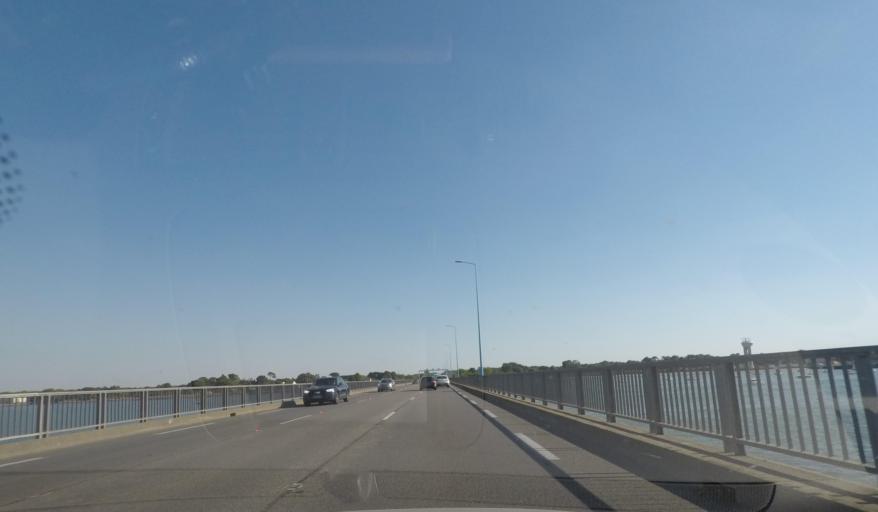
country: FR
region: Pays de la Loire
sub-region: Departement de la Loire-Atlantique
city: Saint-Brevin-les-Pins
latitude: 47.2733
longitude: -2.1634
